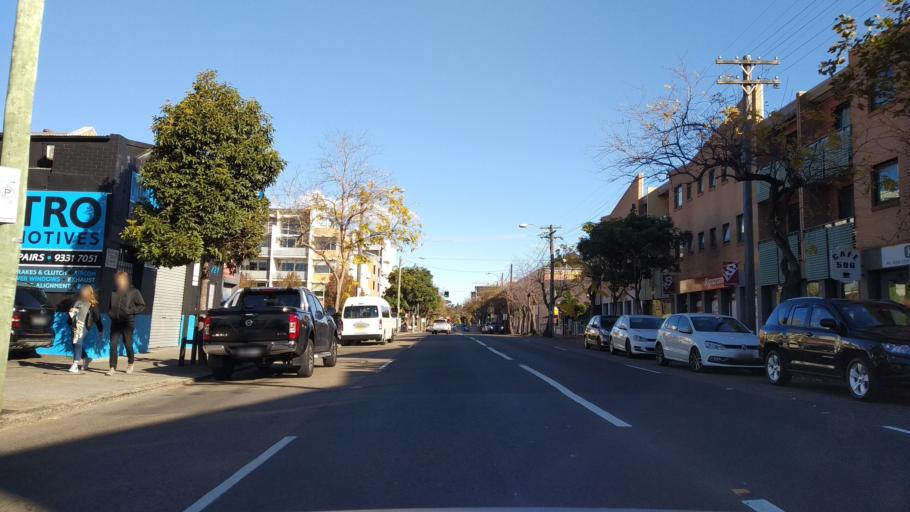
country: AU
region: New South Wales
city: Alexandria
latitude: -33.9134
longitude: 151.2012
